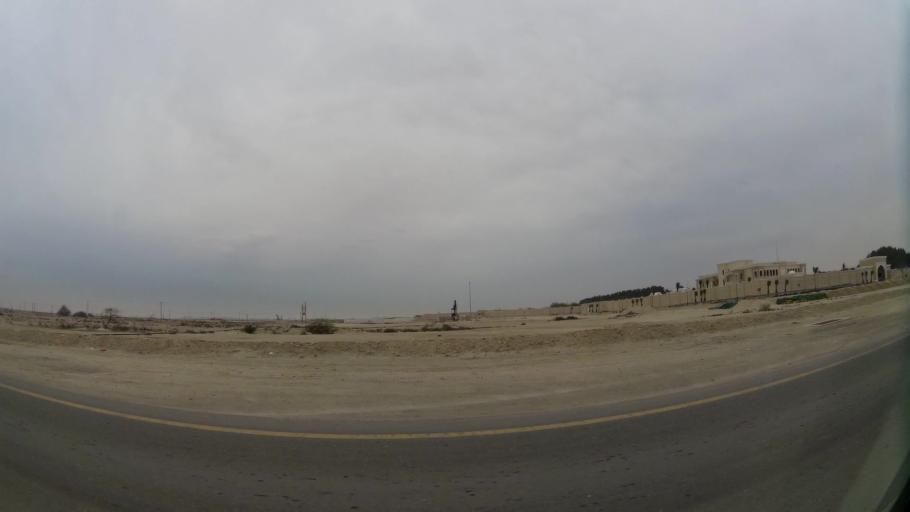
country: BH
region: Northern
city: Ar Rifa'
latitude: 26.0911
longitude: 50.5649
